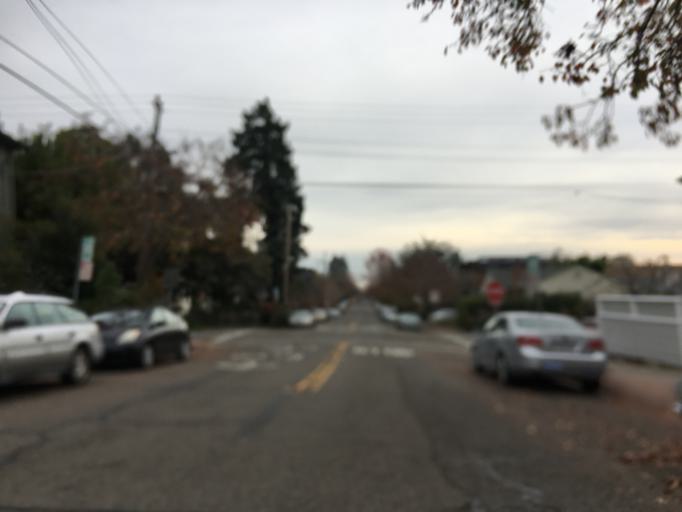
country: US
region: California
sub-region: Alameda County
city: Berkeley
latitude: 37.8803
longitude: -122.2717
